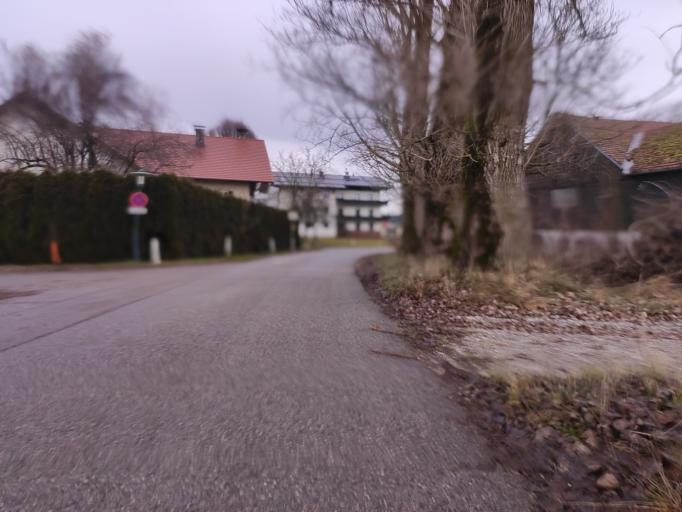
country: AT
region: Salzburg
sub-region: Politischer Bezirk Salzburg-Umgebung
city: Elixhausen
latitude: 47.9026
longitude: 13.0592
